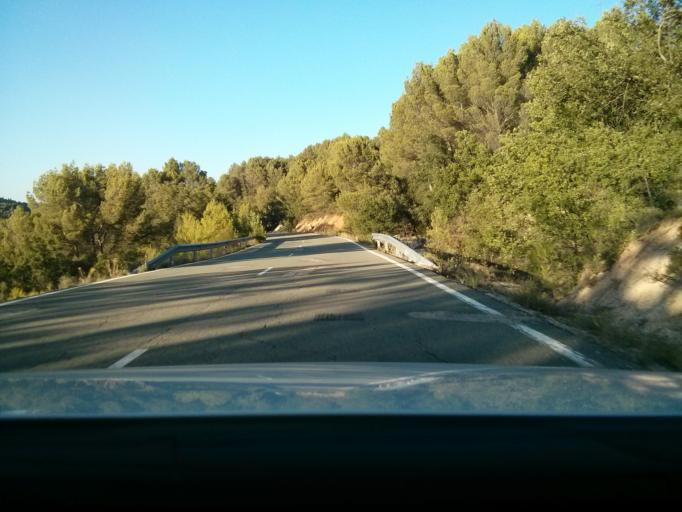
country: ES
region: Castille-La Mancha
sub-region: Provincia de Guadalajara
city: Mantiel
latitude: 40.6206
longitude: -2.6791
